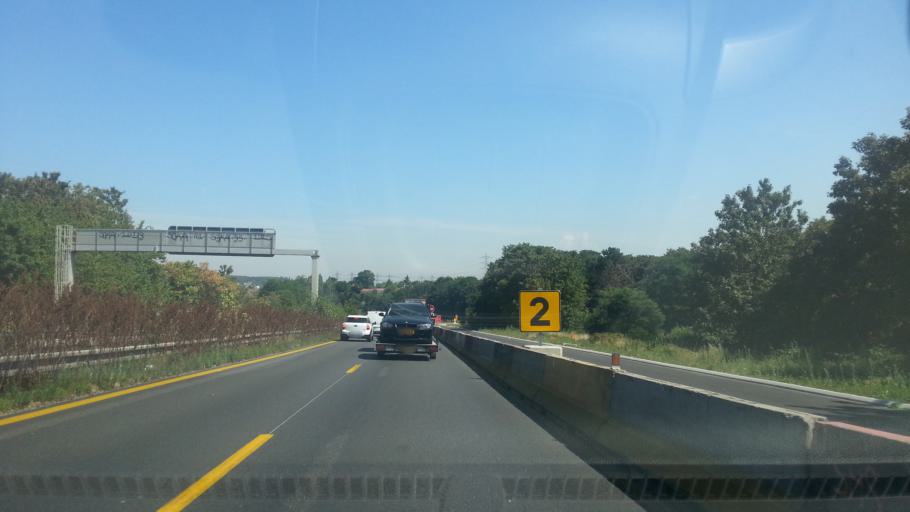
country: FR
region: Ile-de-France
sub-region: Departement de l'Essonne
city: Villebon-sur-Yvette
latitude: 48.6973
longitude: 2.2398
